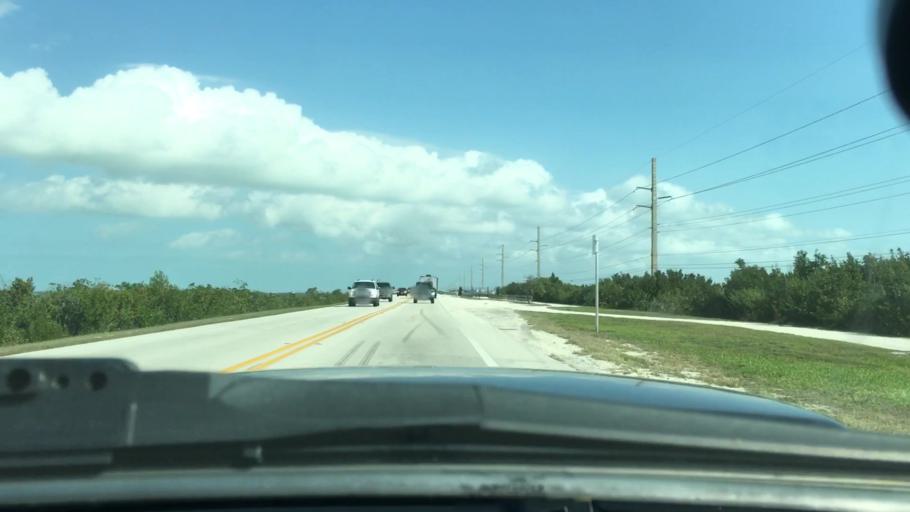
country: US
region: Florida
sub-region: Monroe County
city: Big Coppitt Key
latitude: 24.6307
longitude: -81.5904
